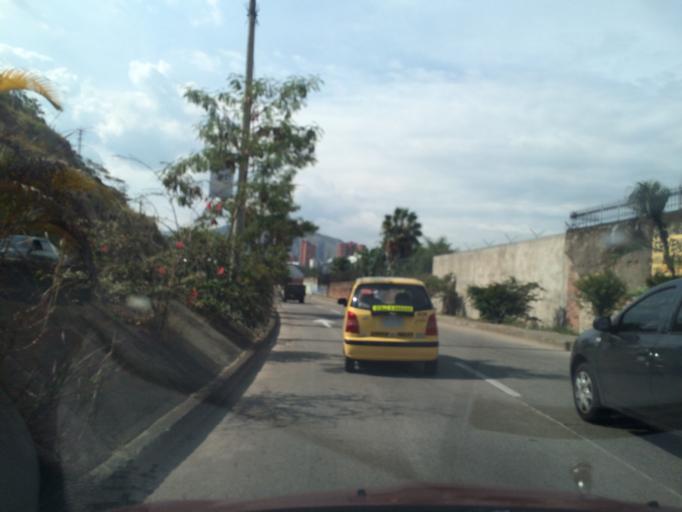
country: CO
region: Valle del Cauca
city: Cali
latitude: 3.4379
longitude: -76.5490
